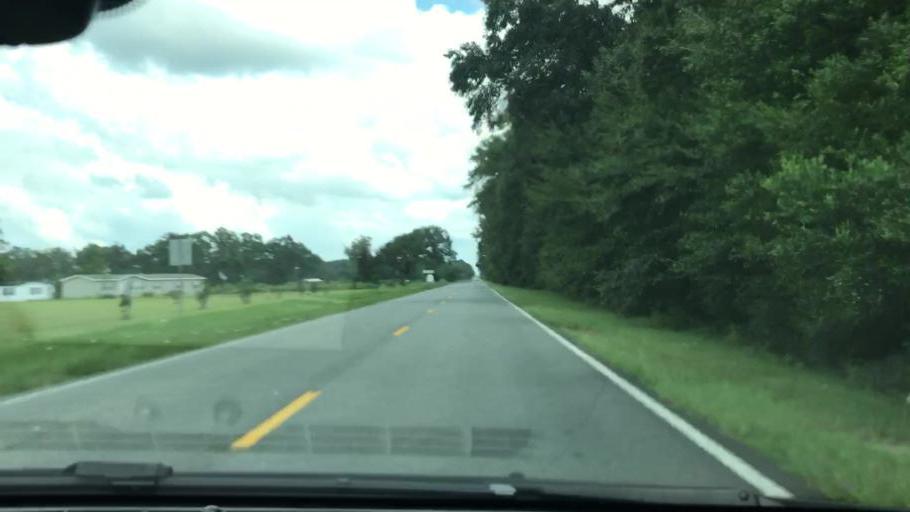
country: US
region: Florida
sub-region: Jackson County
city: Malone
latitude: 30.8855
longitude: -85.1561
